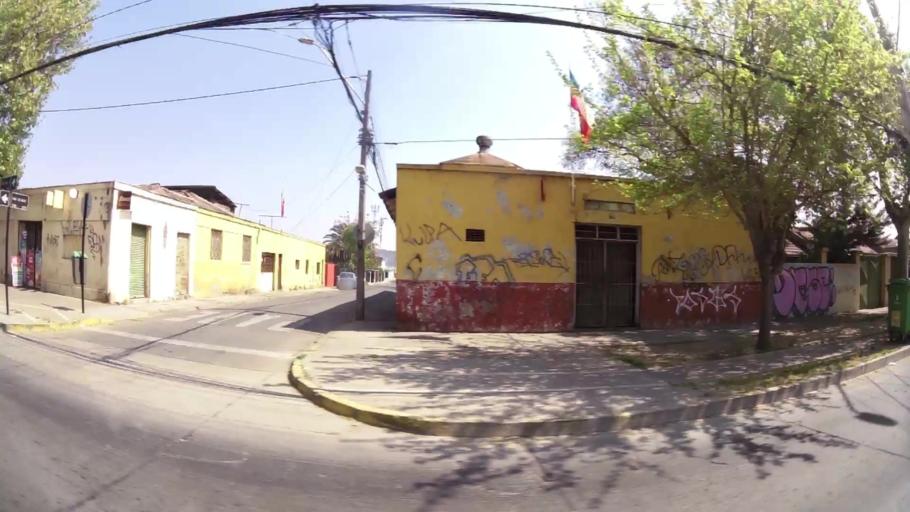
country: CL
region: Santiago Metropolitan
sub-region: Provincia de Santiago
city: Santiago
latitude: -33.4712
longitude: -70.6650
